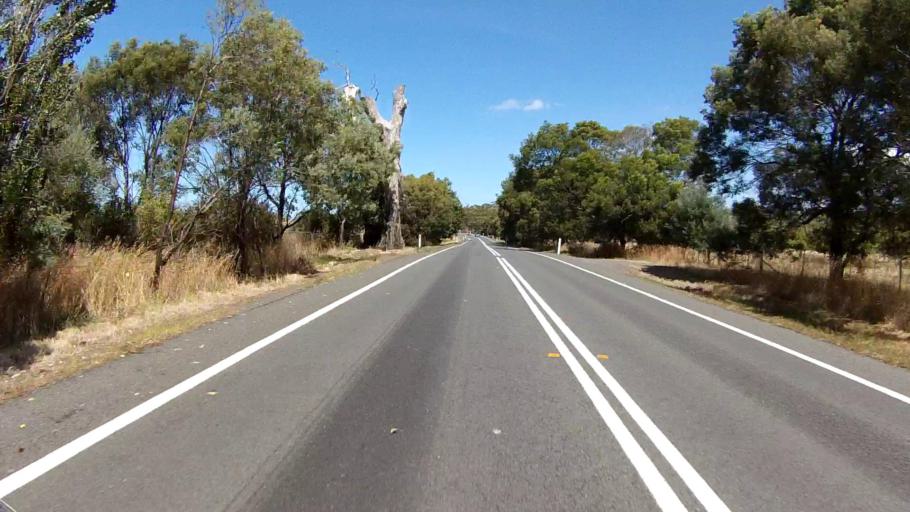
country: AU
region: Tasmania
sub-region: Break O'Day
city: St Helens
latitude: -42.0743
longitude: 148.0671
